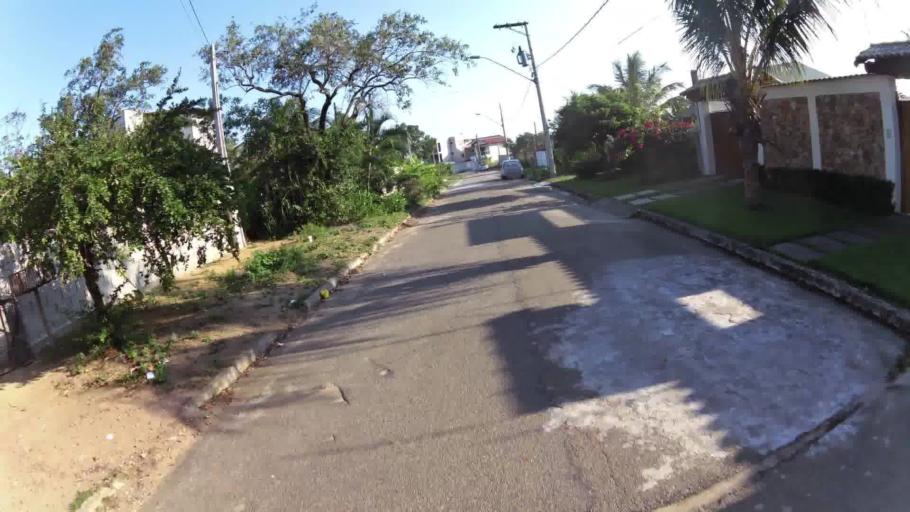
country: BR
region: Espirito Santo
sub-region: Guarapari
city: Guarapari
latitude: -20.7252
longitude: -40.5338
